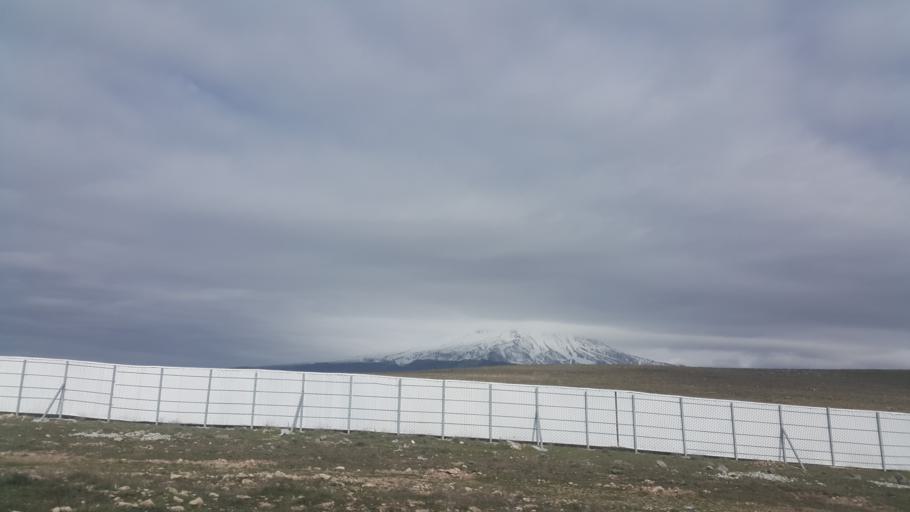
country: TR
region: Aksaray
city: Taspinar
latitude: 38.1389
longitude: 34.0346
